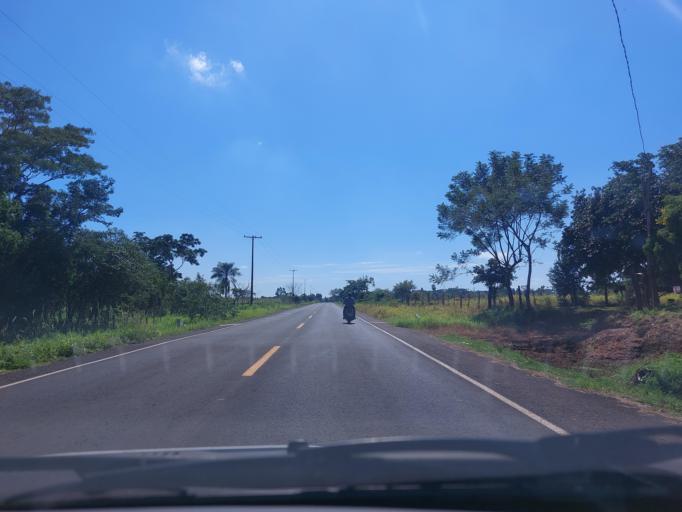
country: PY
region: San Pedro
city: Guayaybi
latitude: -24.5764
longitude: -56.5196
